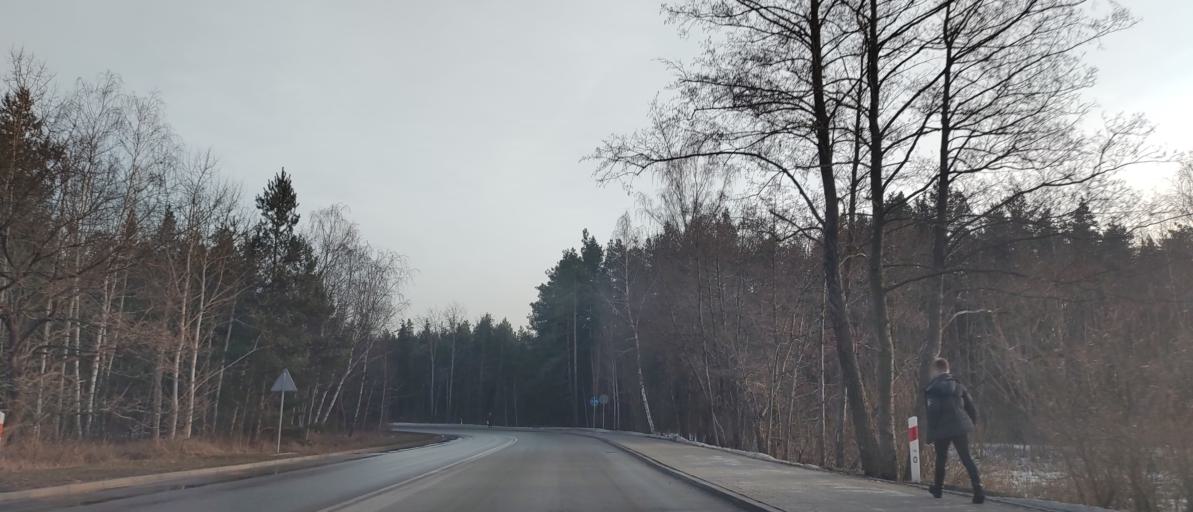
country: PL
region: Masovian Voivodeship
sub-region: Powiat bialobrzeski
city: Bialobrzegi
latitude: 51.6448
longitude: 20.9329
